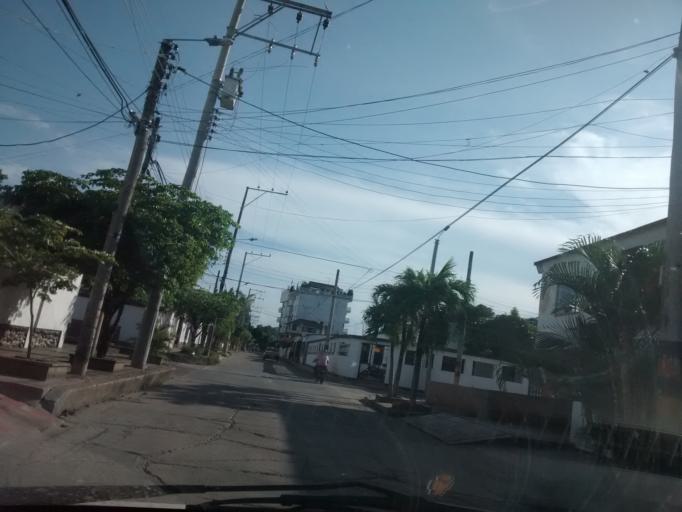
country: CO
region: Cundinamarca
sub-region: Girardot
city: Girardot City
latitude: 4.3074
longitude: -74.7995
